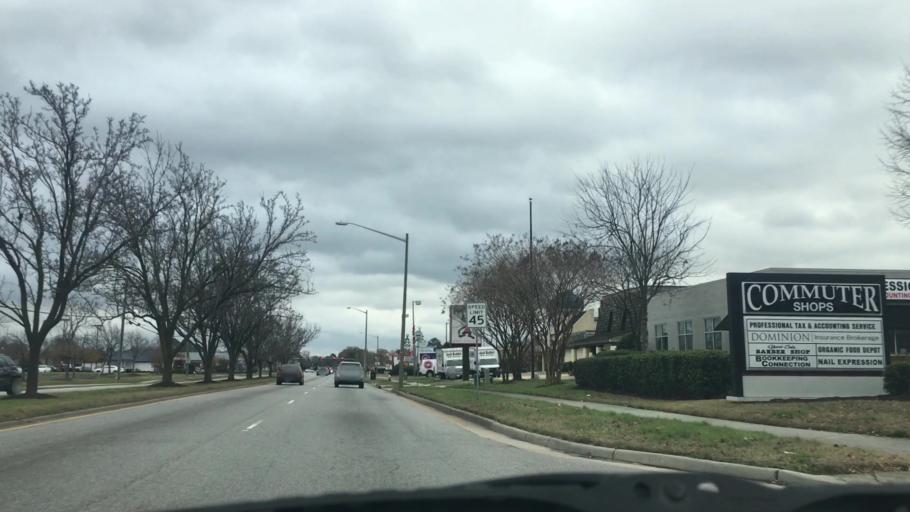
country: US
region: Virginia
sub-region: City of Virginia Beach
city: Virginia Beach
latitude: 36.8215
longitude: -76.1237
